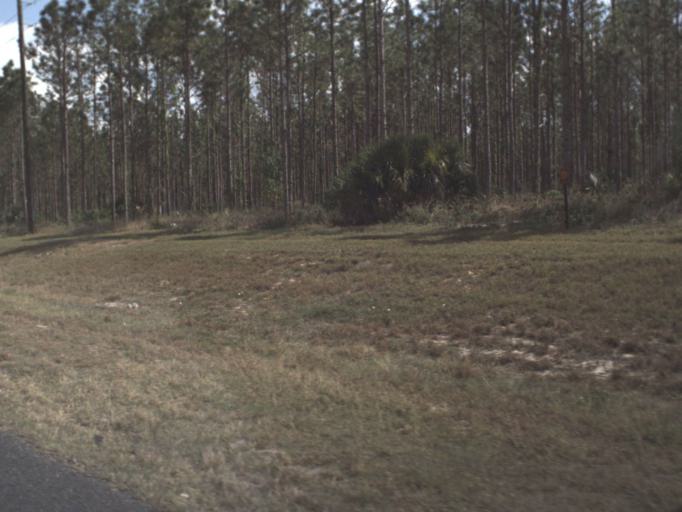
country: US
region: Florida
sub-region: Lake County
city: Mascotte
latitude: 28.6535
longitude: -81.8406
